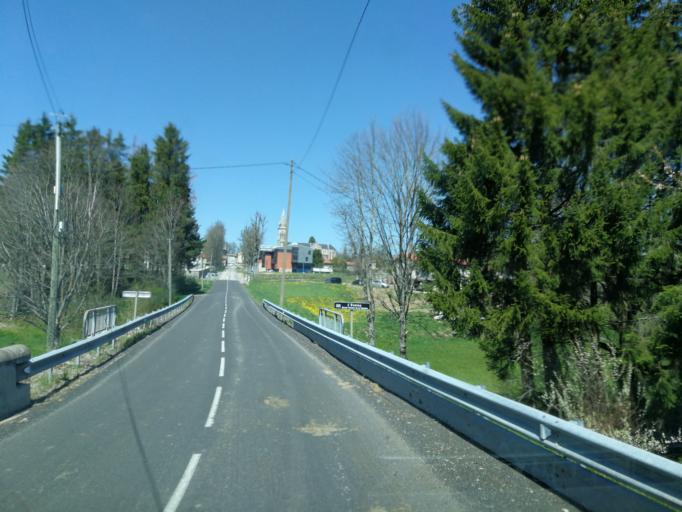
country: FR
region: Rhone-Alpes
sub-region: Departement de la Loire
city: Marlhes
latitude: 45.2790
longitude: 4.3958
